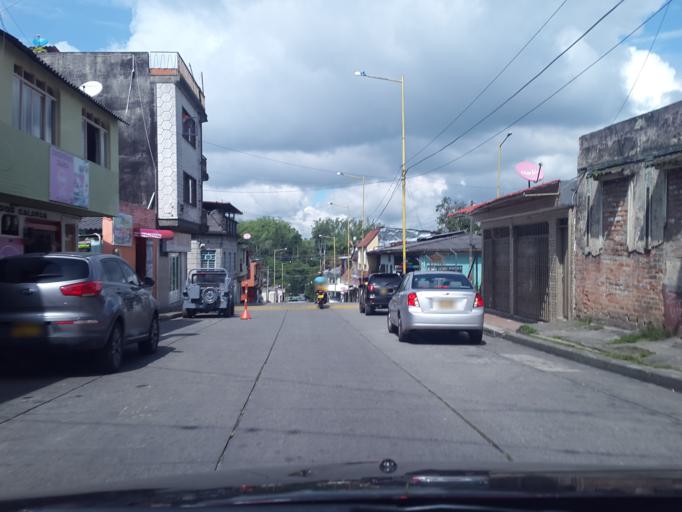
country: CO
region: Quindio
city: Calarca
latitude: 4.5316
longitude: -75.6423
